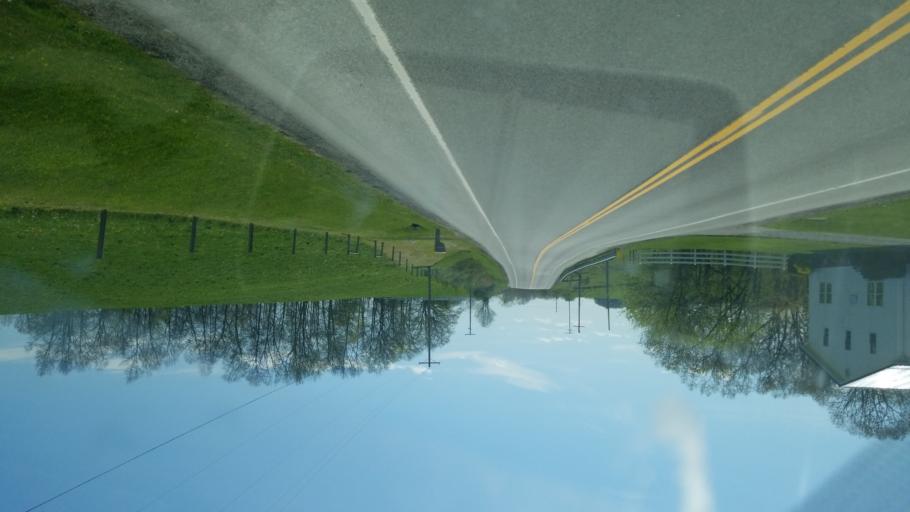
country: US
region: Ohio
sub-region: Tuscarawas County
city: Sugarcreek
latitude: 40.4451
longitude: -81.7247
